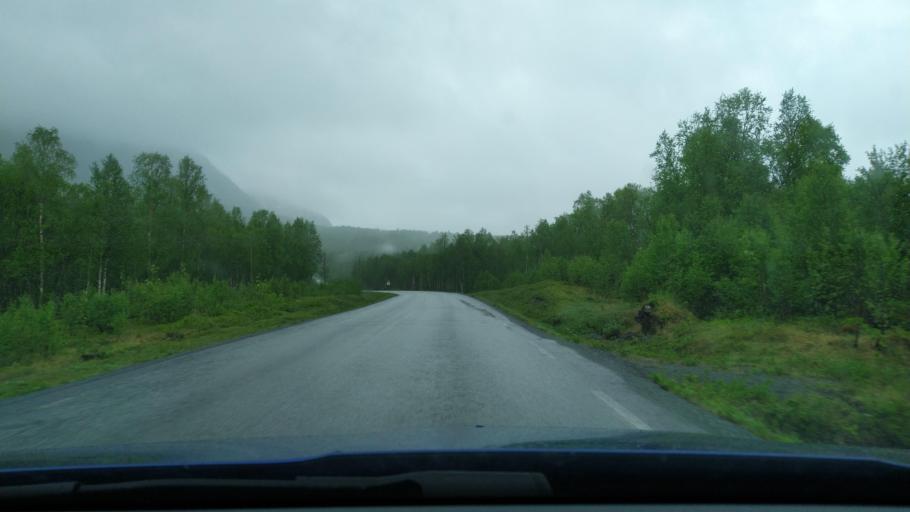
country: NO
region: Troms
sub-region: Dyroy
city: Brostadbotn
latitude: 69.0229
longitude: 17.7372
